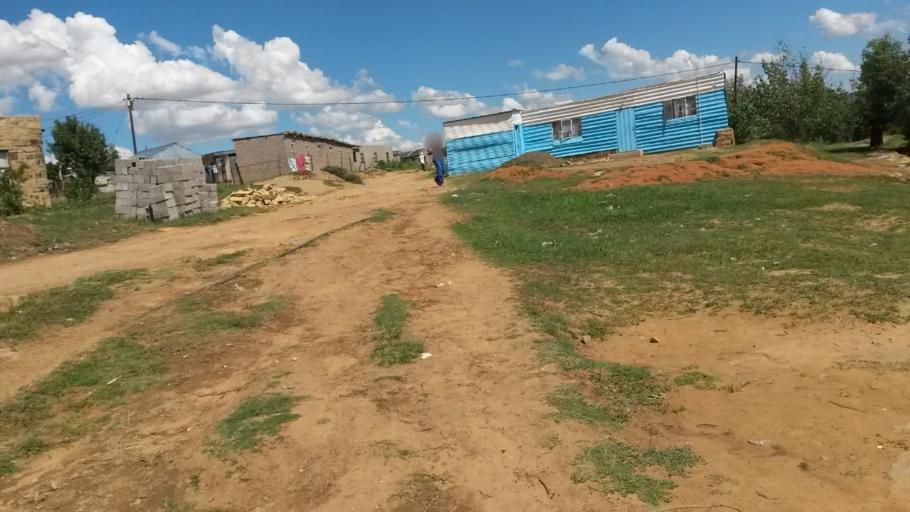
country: LS
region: Maseru
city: Maseru
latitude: -29.3688
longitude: 27.5037
